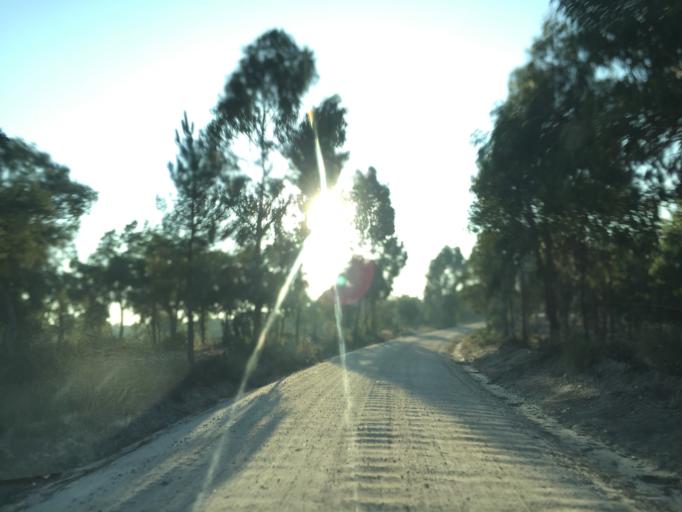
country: PT
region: Portalegre
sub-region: Ponte de Sor
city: Santo Andre
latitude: 39.0815
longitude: -8.3871
